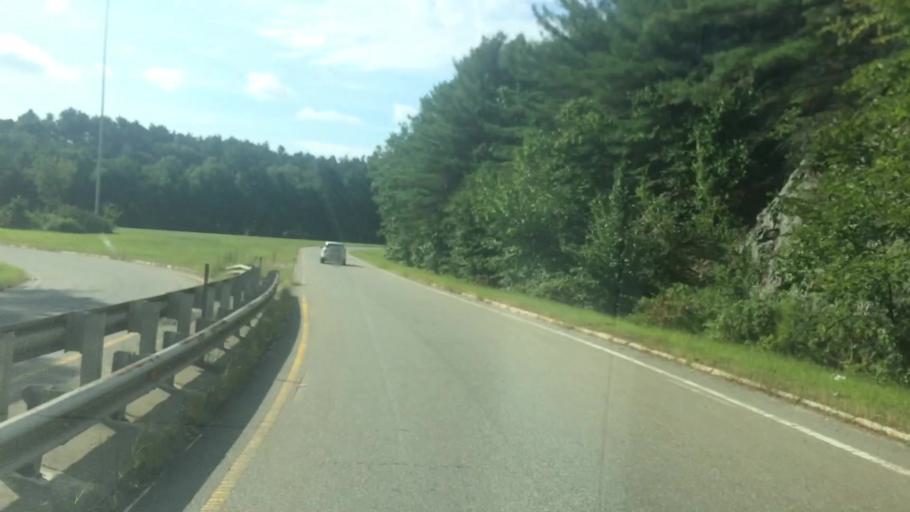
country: US
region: Massachusetts
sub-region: Worcester County
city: Harvard
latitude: 42.4864
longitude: -71.5476
